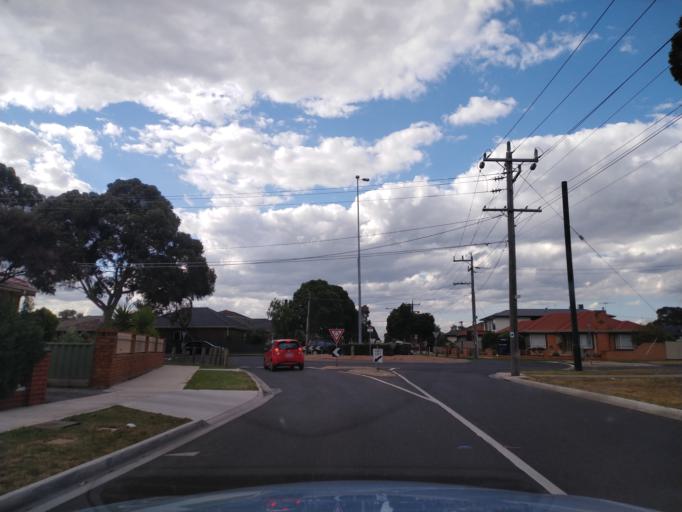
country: AU
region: Victoria
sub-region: Hobsons Bay
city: Altona North
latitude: -37.8397
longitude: 144.8550
